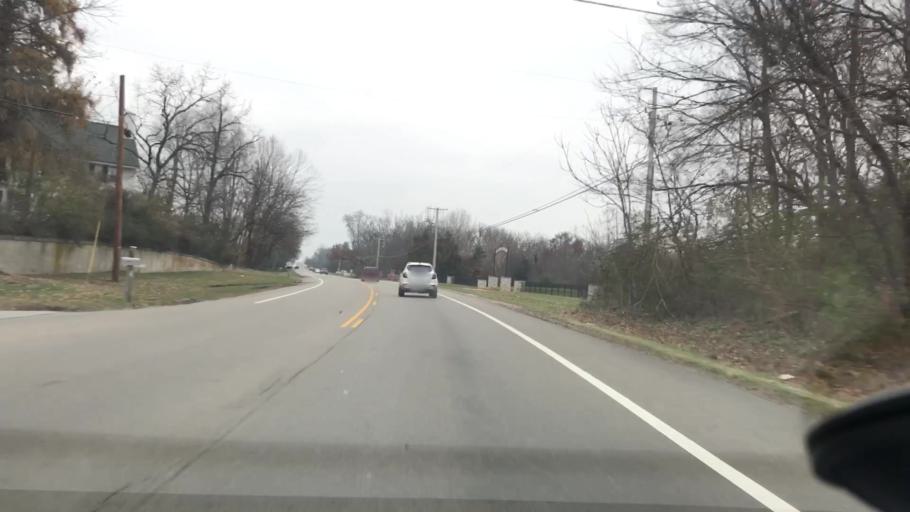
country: US
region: Ohio
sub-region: Greene County
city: Yellow Springs
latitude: 39.8109
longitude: -83.8820
